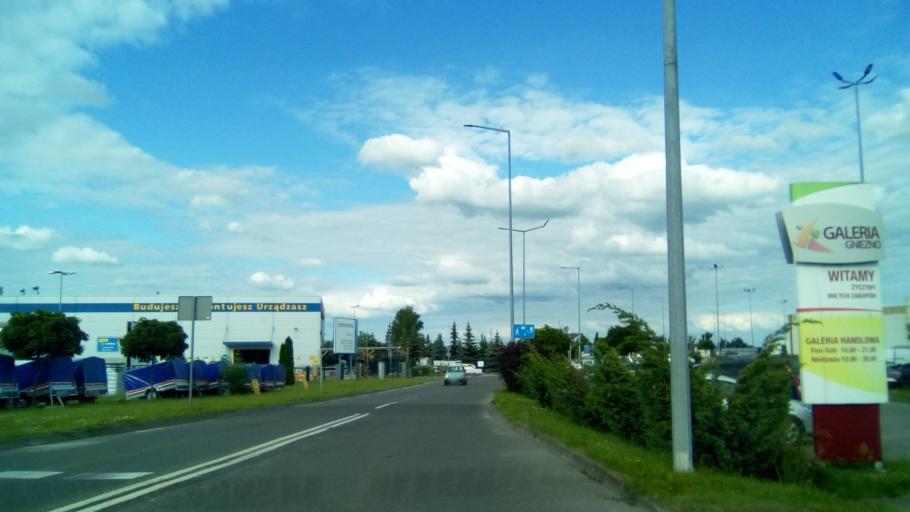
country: PL
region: Greater Poland Voivodeship
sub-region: Powiat gnieznienski
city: Gniezno
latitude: 52.5617
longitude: 17.6102
